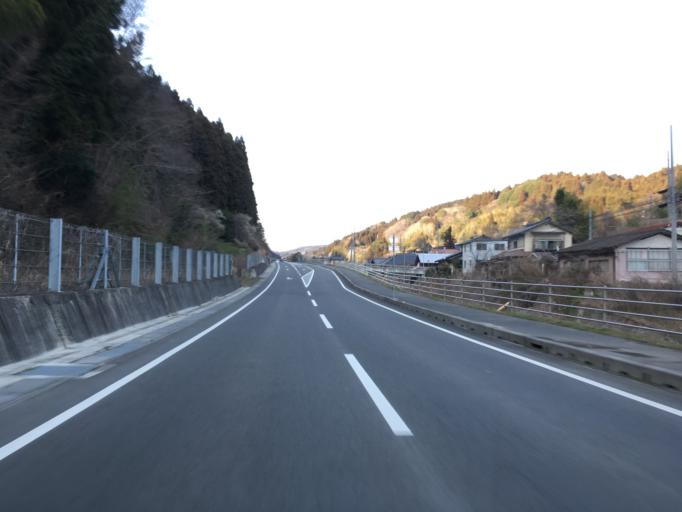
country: JP
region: Ibaraki
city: Daigo
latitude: 36.7094
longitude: 140.4650
